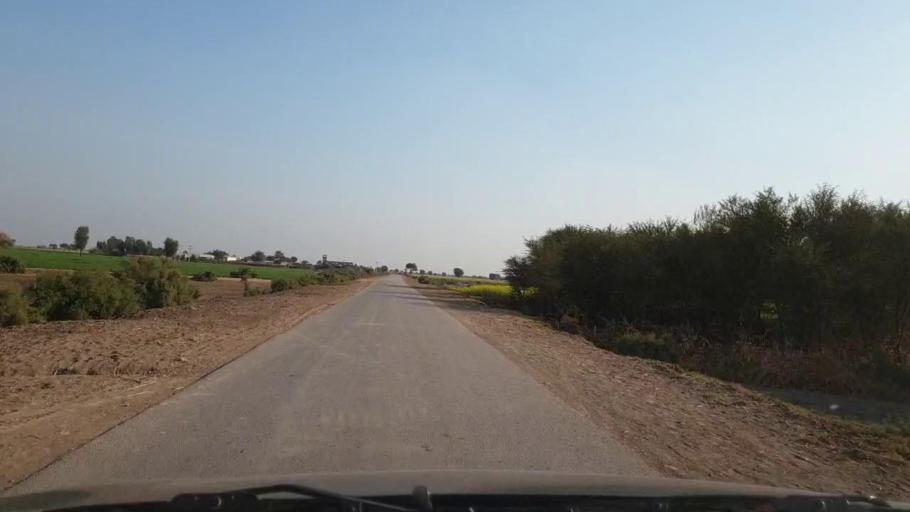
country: PK
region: Sindh
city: Jhol
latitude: 25.9451
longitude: 68.9064
